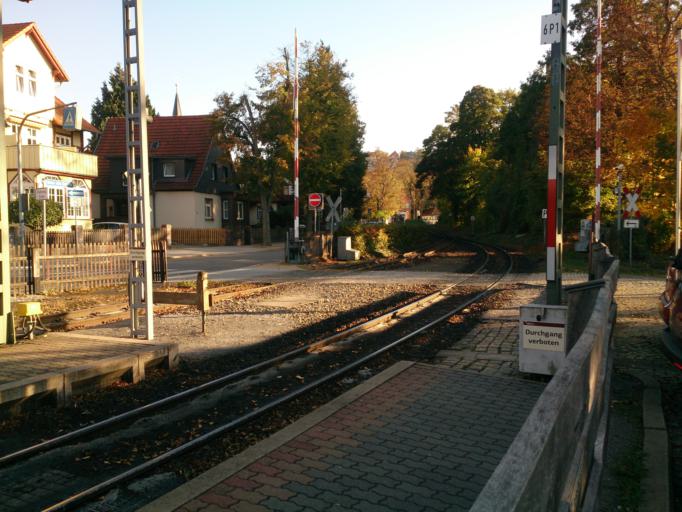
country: DE
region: Saxony-Anhalt
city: Wernigerode
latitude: 51.8338
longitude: 10.7802
